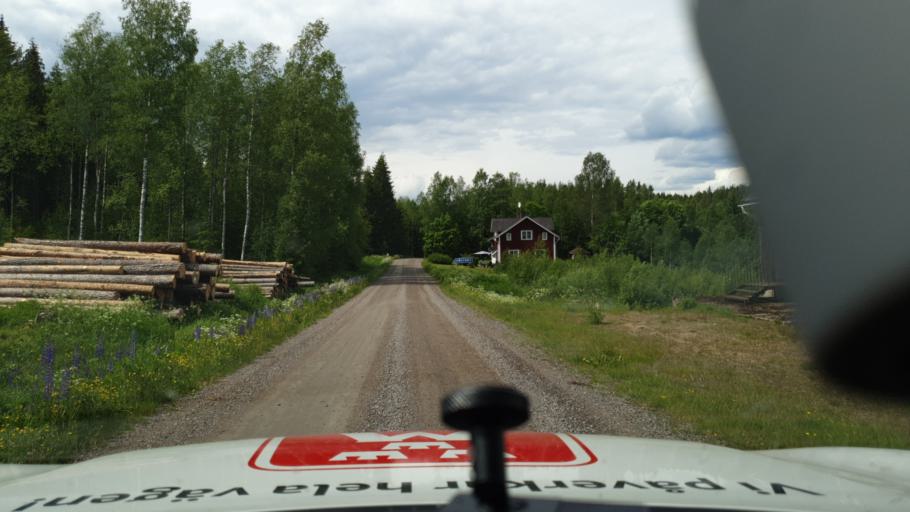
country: SE
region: Vaermland
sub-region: Torsby Kommun
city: Torsby
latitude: 59.9819
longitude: 12.8366
